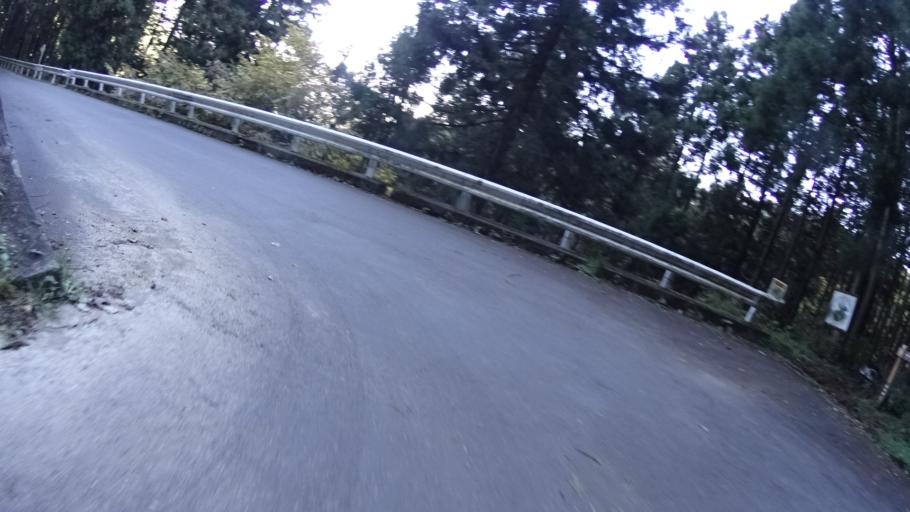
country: JP
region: Yamanashi
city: Uenohara
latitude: 35.6571
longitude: 139.1703
